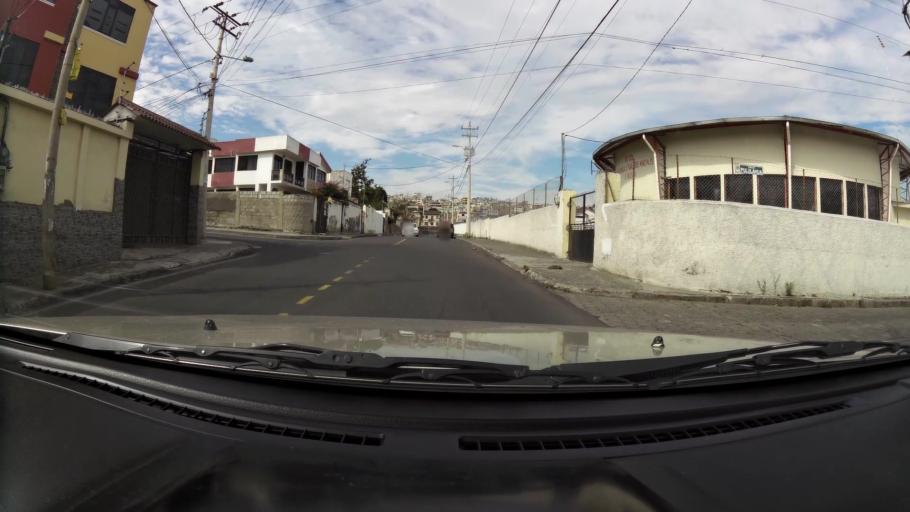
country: EC
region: Tungurahua
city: Ambato
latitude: -1.2442
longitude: -78.6208
